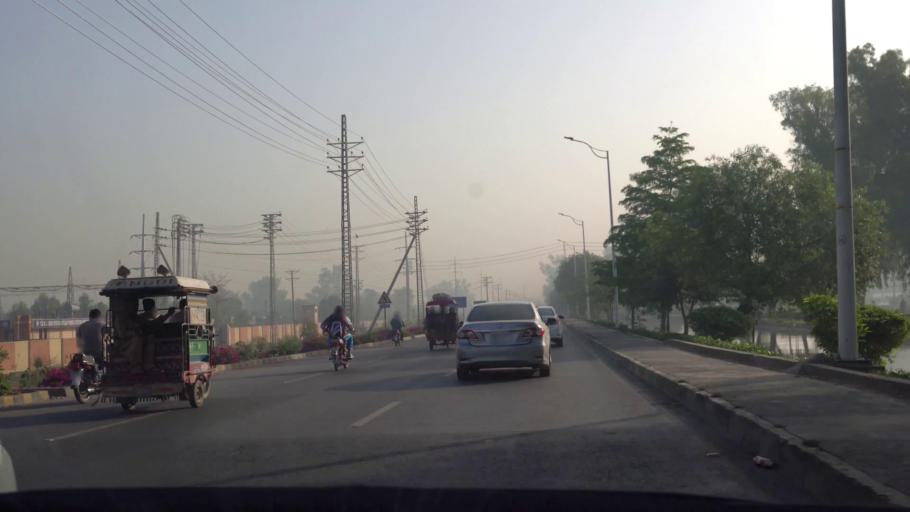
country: PK
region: Punjab
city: Faisalabad
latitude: 31.4440
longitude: 73.1385
